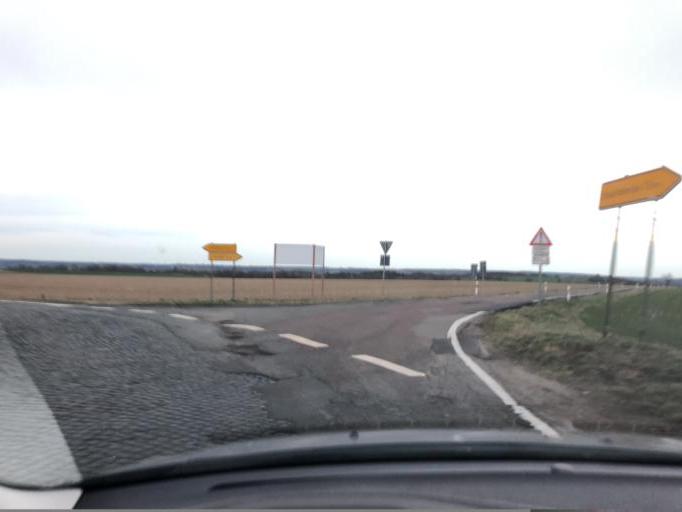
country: DE
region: Saxony-Anhalt
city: Laucha
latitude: 51.2018
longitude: 11.6591
